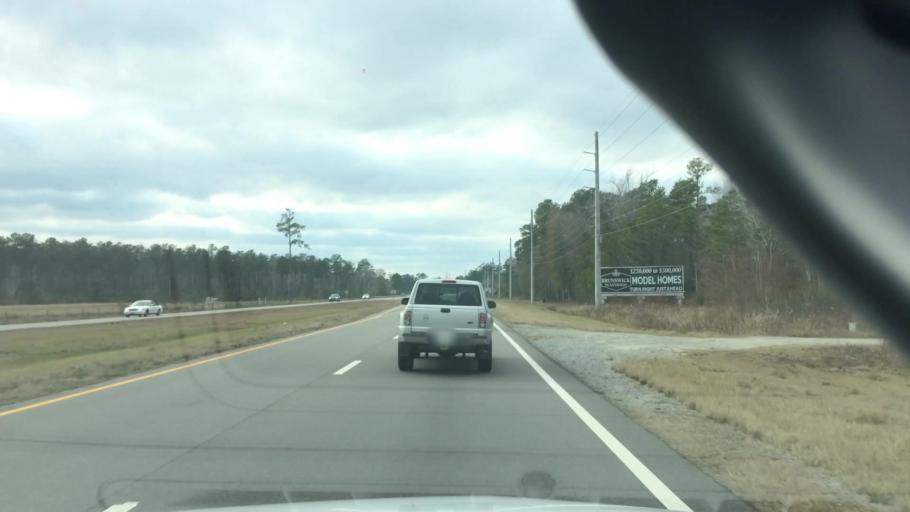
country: US
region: North Carolina
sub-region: Brunswick County
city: Carolina Shores
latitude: 33.9381
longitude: -78.5587
